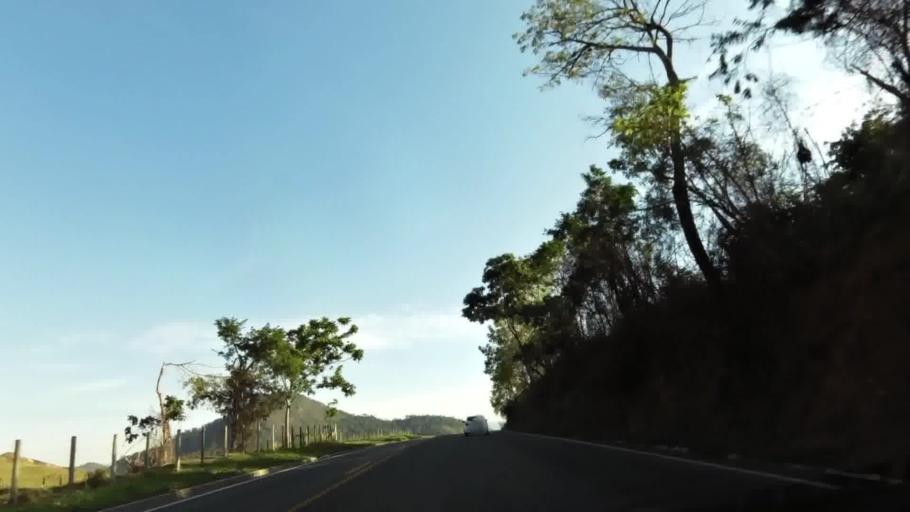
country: BR
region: Espirito Santo
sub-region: Viana
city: Viana
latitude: -20.4937
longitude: -40.4768
